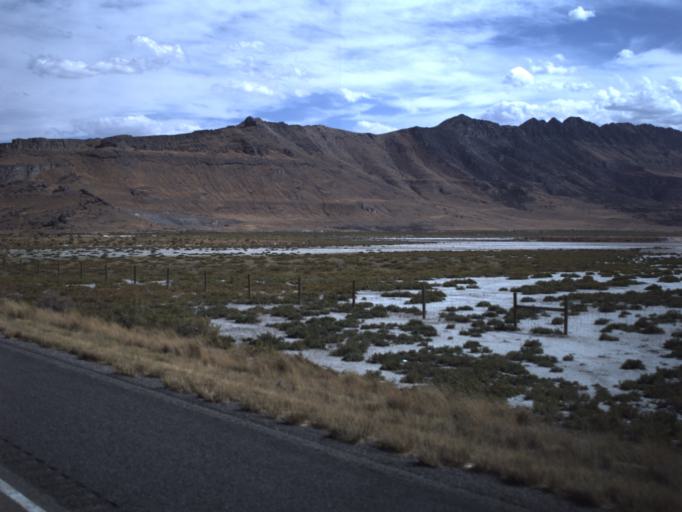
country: US
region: Utah
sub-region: Tooele County
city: Grantsville
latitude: 40.7466
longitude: -112.6625
